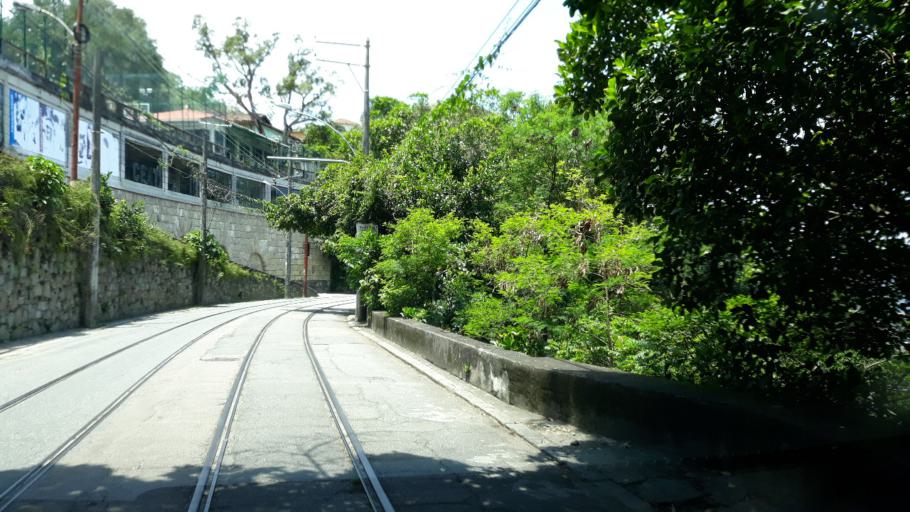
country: BR
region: Rio de Janeiro
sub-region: Rio De Janeiro
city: Rio de Janeiro
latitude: -22.9384
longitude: -43.2068
